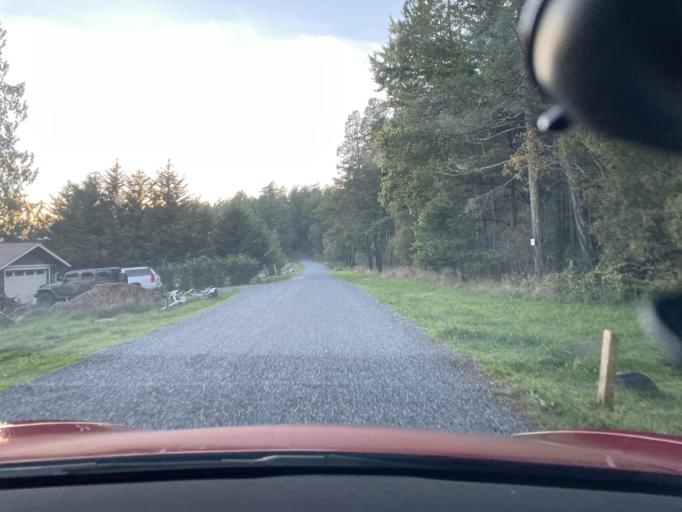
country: US
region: Washington
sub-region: San Juan County
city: Friday Harbor
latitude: 48.6139
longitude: -123.1438
